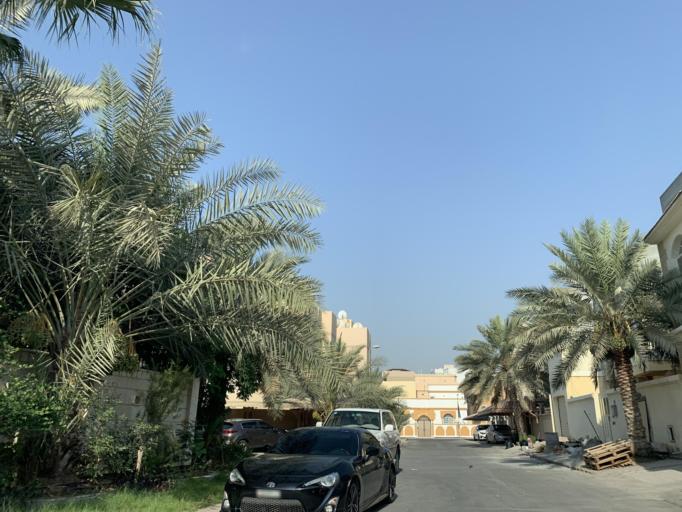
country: BH
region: Manama
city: Jidd Hafs
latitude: 26.1962
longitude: 50.5157
